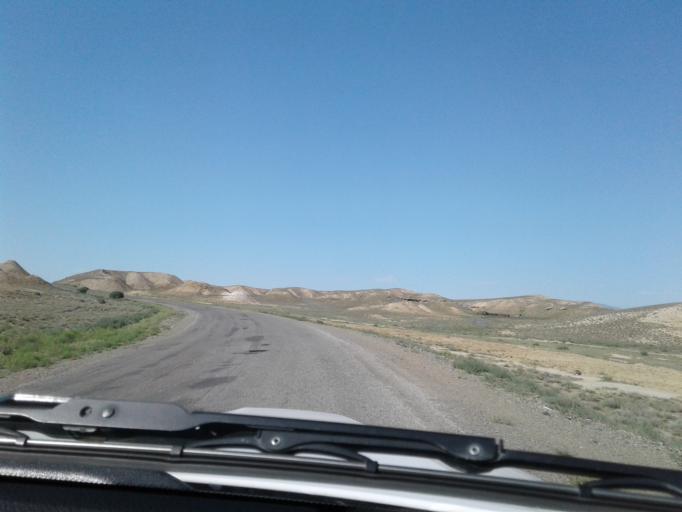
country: TM
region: Balkan
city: Magtymguly
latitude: 38.6733
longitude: 56.2940
